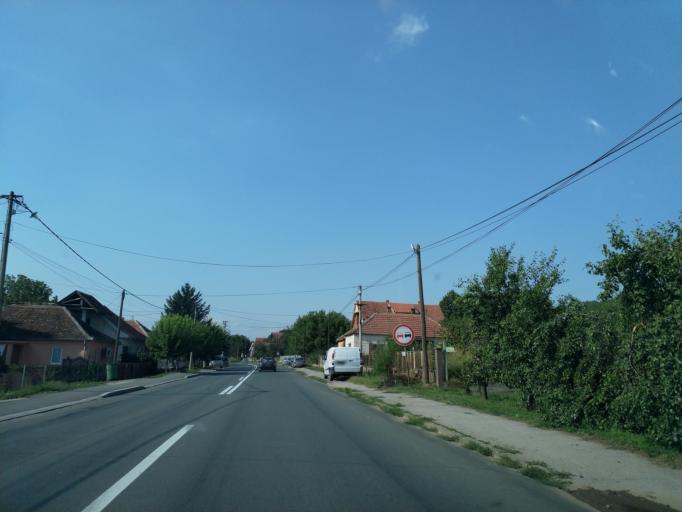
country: RS
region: Central Serbia
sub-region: Rasinski Okrug
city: Cicevac
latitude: 43.7301
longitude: 21.4435
